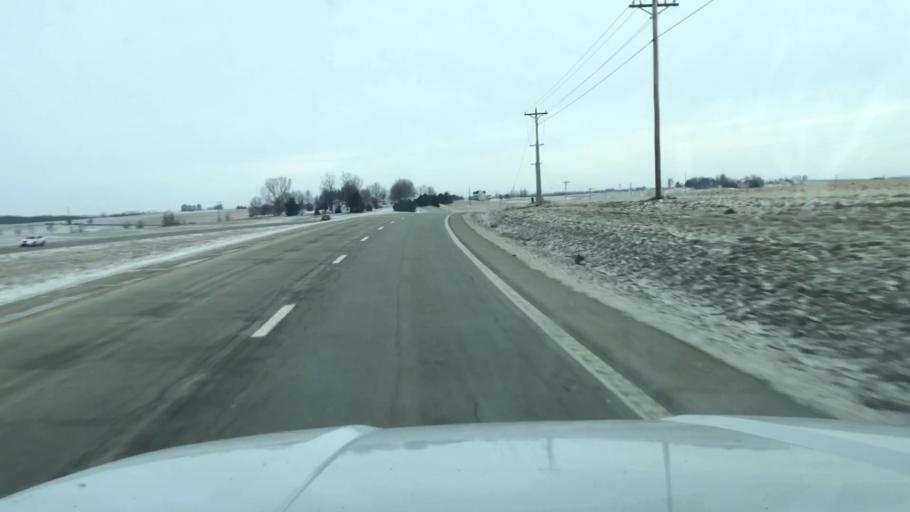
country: US
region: Missouri
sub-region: Andrew County
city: Savannah
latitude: 39.9831
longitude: -94.8795
